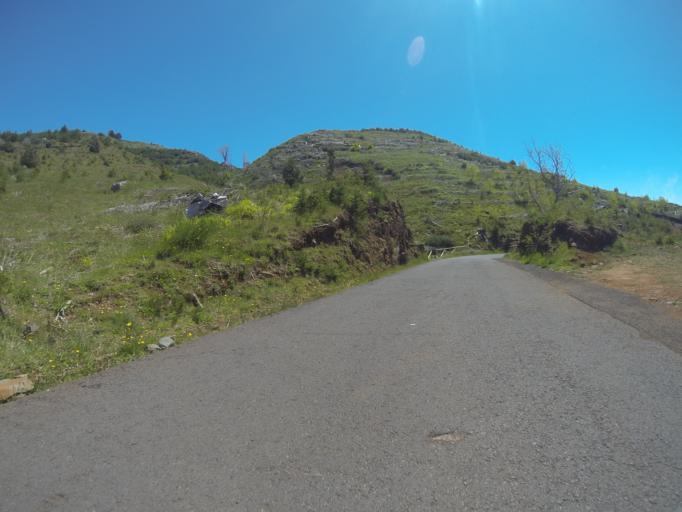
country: PT
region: Madeira
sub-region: Funchal
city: Nossa Senhora do Monte
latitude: 32.7017
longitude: -16.9141
